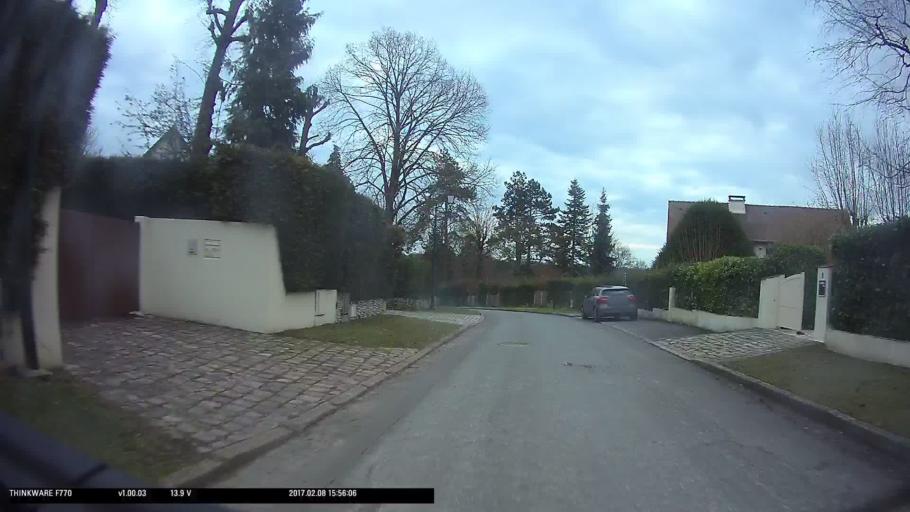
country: FR
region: Ile-de-France
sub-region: Departement du Val-d'Oise
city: Vigny
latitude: 49.0782
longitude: 1.9349
